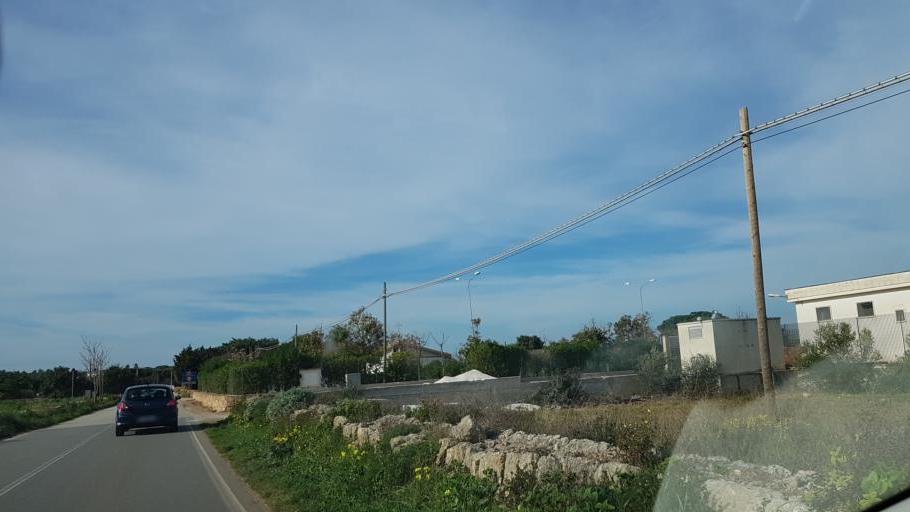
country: IT
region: Apulia
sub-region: Provincia di Brindisi
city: Fasano
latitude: 40.9020
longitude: 17.3521
